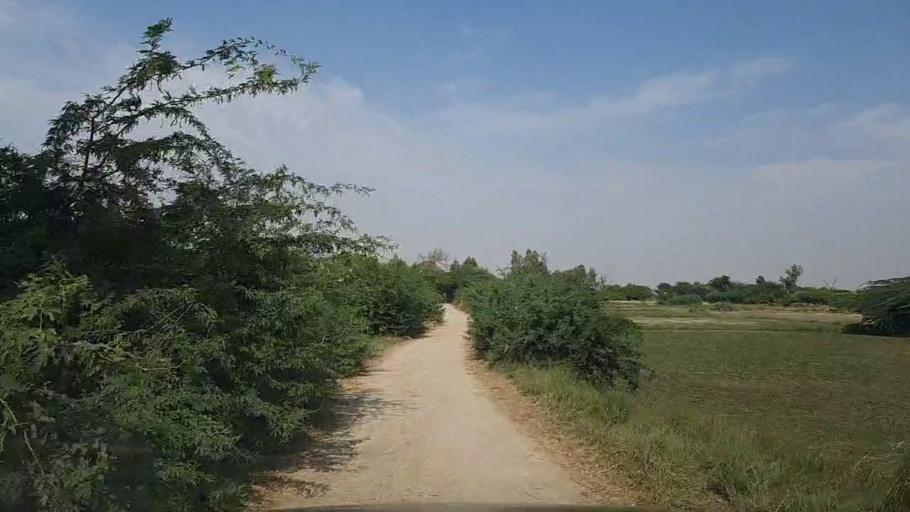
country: PK
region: Sindh
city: Thatta
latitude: 24.8006
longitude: 67.8643
